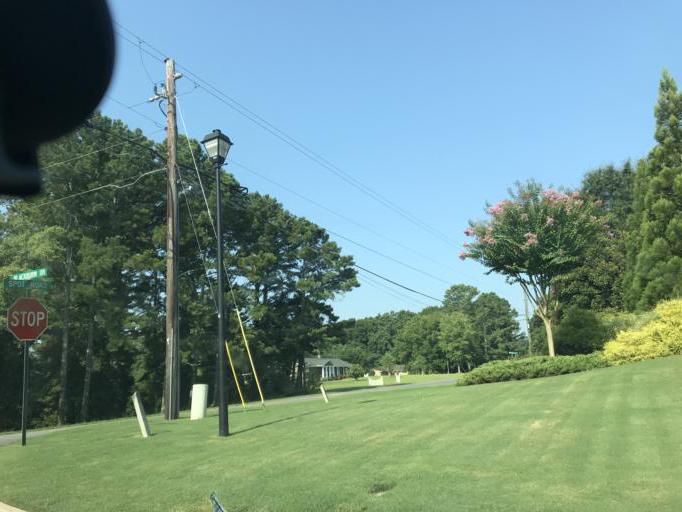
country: US
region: Georgia
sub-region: Forsyth County
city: Cumming
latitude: 34.2627
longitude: -84.1147
